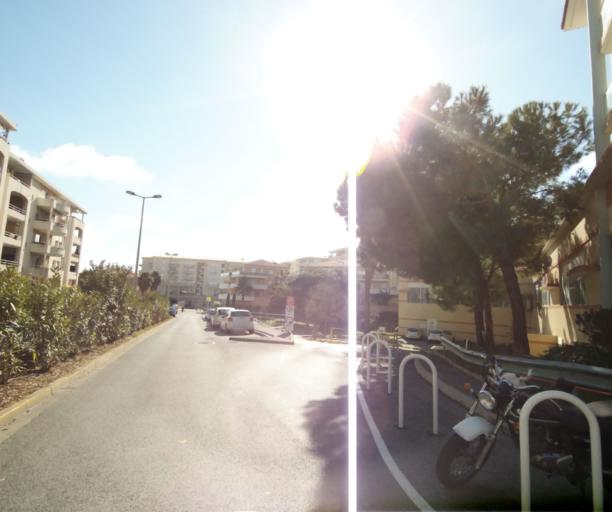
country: FR
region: Provence-Alpes-Cote d'Azur
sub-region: Departement des Alpes-Maritimes
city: Vallauris
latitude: 43.5736
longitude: 7.0909
